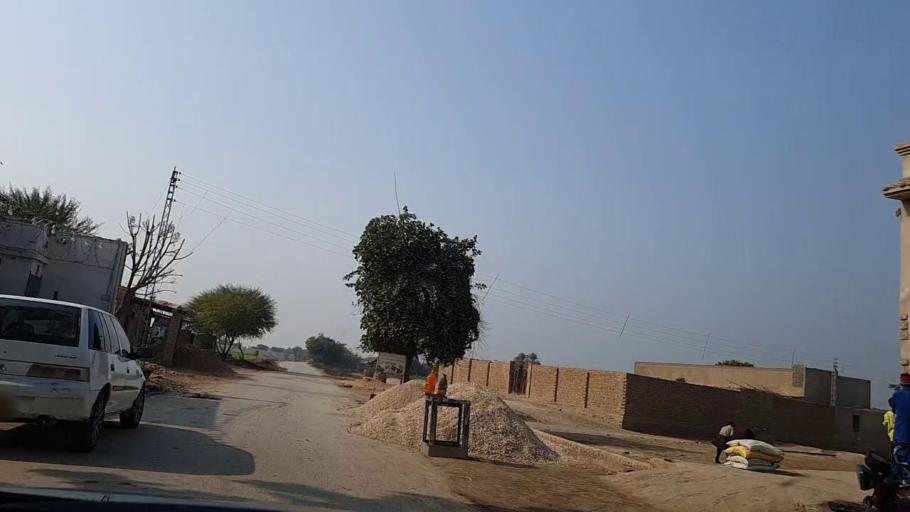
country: PK
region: Sindh
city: Sann
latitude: 26.1492
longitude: 68.1294
